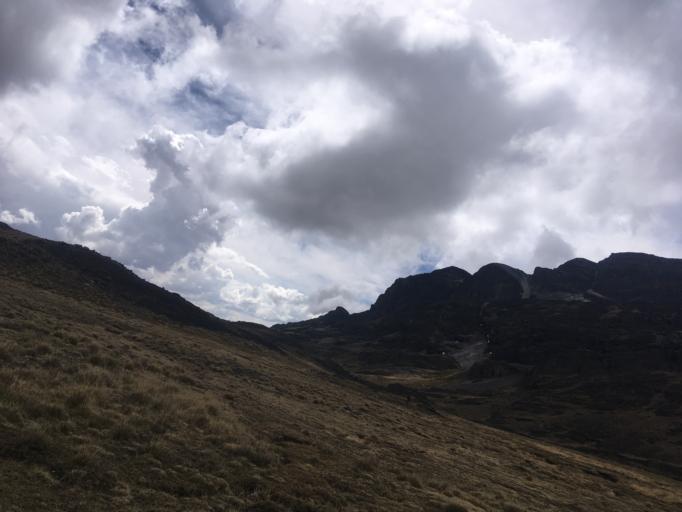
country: BO
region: La Paz
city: La Paz
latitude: -16.3937
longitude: -67.9614
